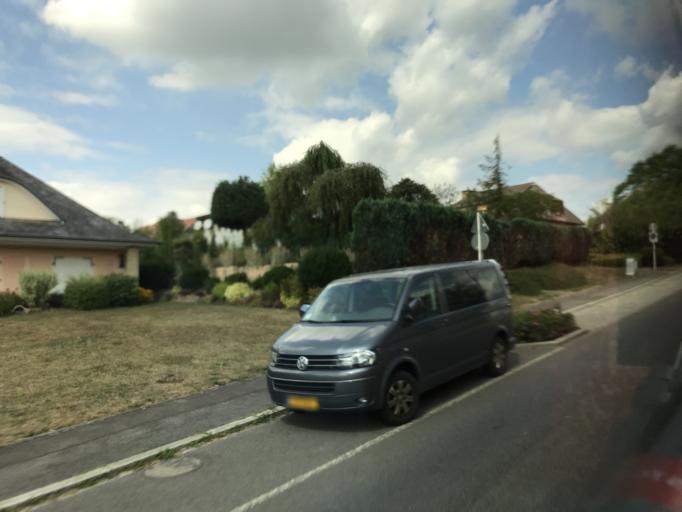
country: LU
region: Luxembourg
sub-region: Canton d'Esch-sur-Alzette
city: Frisange
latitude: 49.5227
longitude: 6.1853
